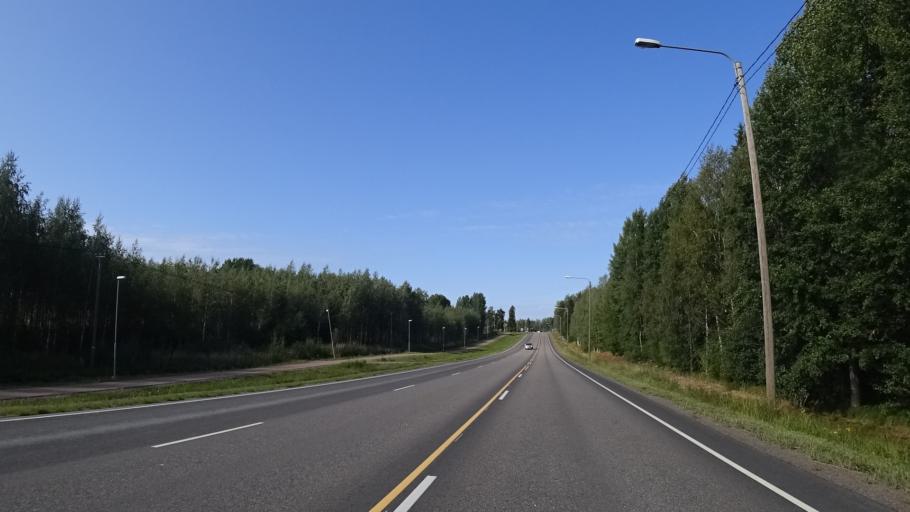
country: FI
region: Kymenlaakso
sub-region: Kotka-Hamina
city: Virojoki
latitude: 60.5881
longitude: 27.7342
